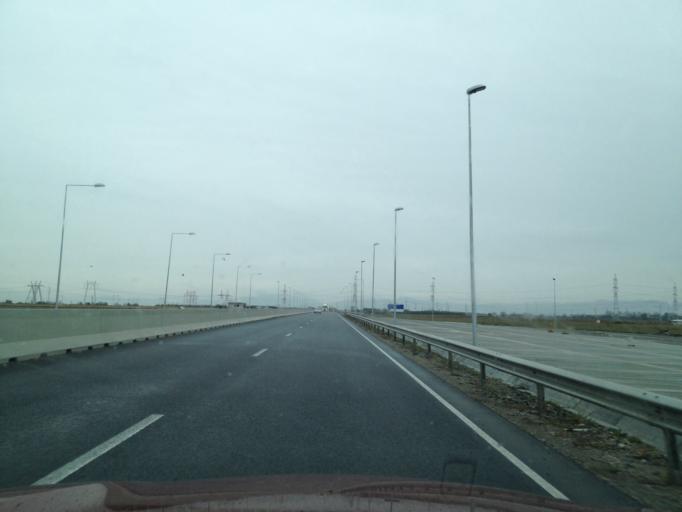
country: RO
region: Brasov
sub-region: Comuna Sanpetru
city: Sanpetru
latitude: 45.6886
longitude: 25.6358
